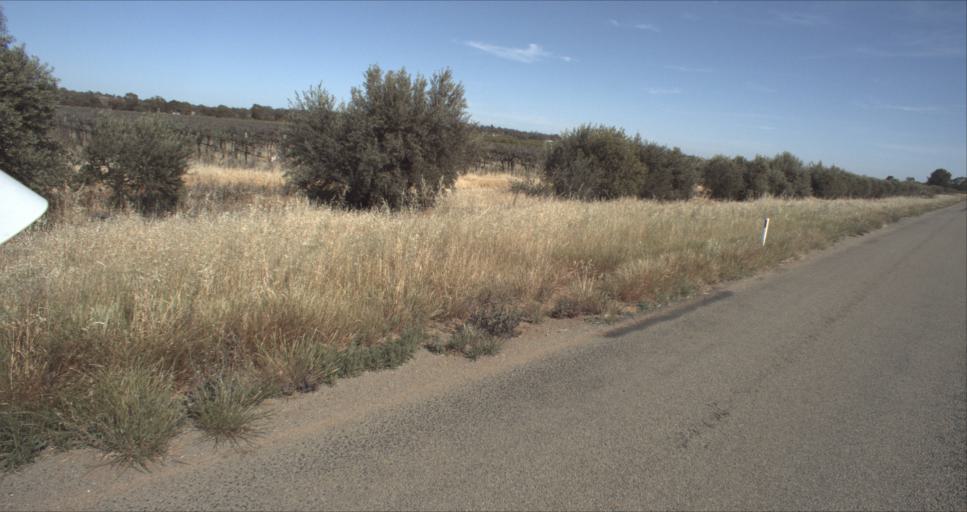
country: AU
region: New South Wales
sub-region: Leeton
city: Leeton
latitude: -34.5703
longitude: 146.4739
